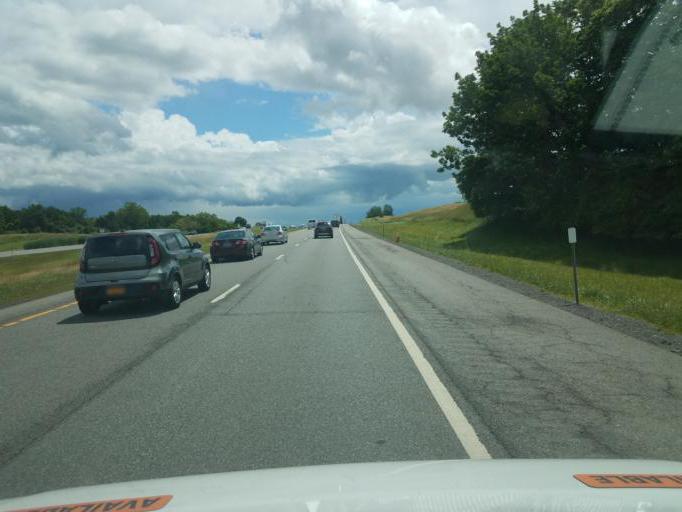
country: US
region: New York
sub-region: Monroe County
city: Pittsford
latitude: 43.0429
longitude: -77.5515
